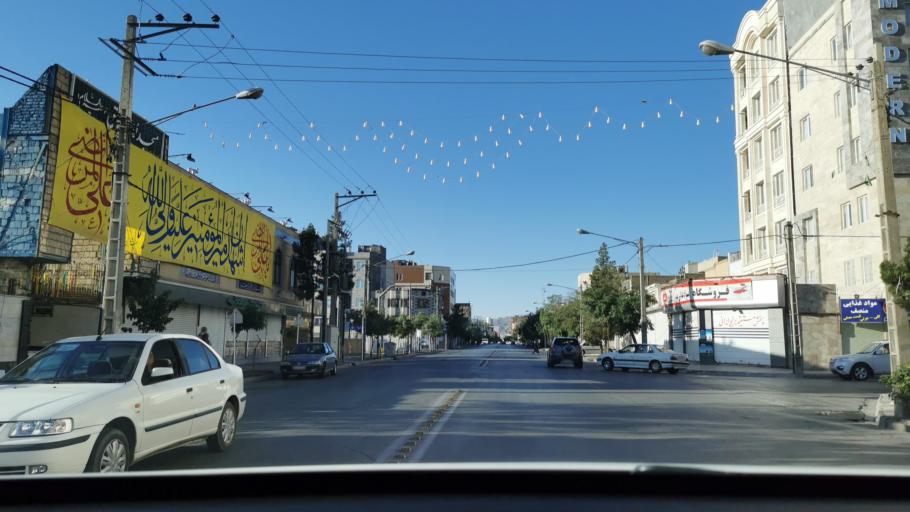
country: IR
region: Razavi Khorasan
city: Mashhad
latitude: 36.3551
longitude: 59.4973
